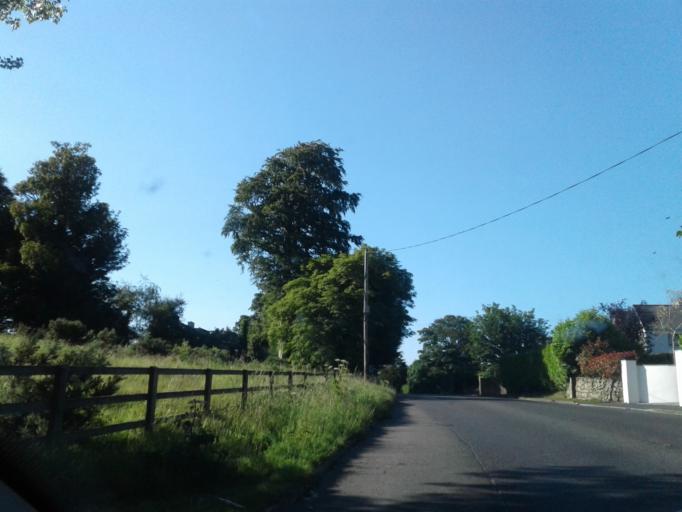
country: IE
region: Leinster
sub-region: Wicklow
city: Enniskerry
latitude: 53.2234
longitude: -6.1816
